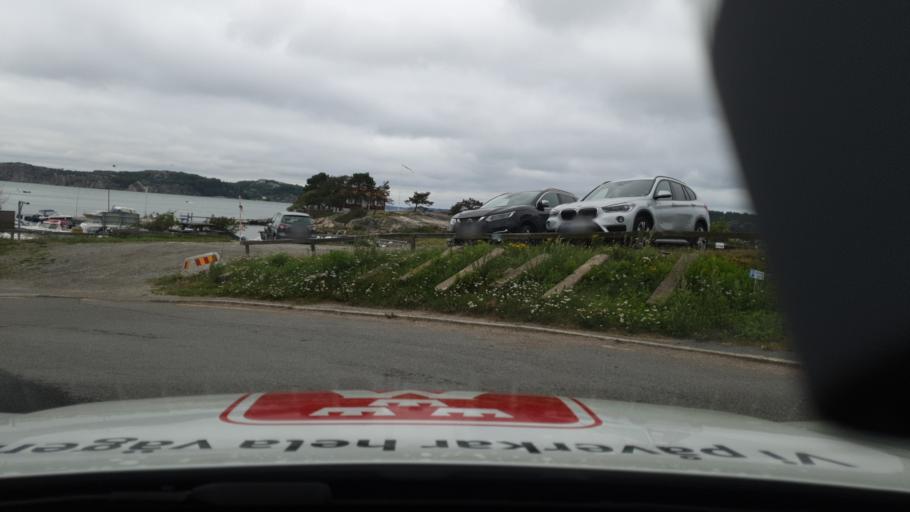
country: SE
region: Vaestra Goetaland
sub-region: Kungalvs Kommun
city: Kode
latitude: 57.9220
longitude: 11.7543
